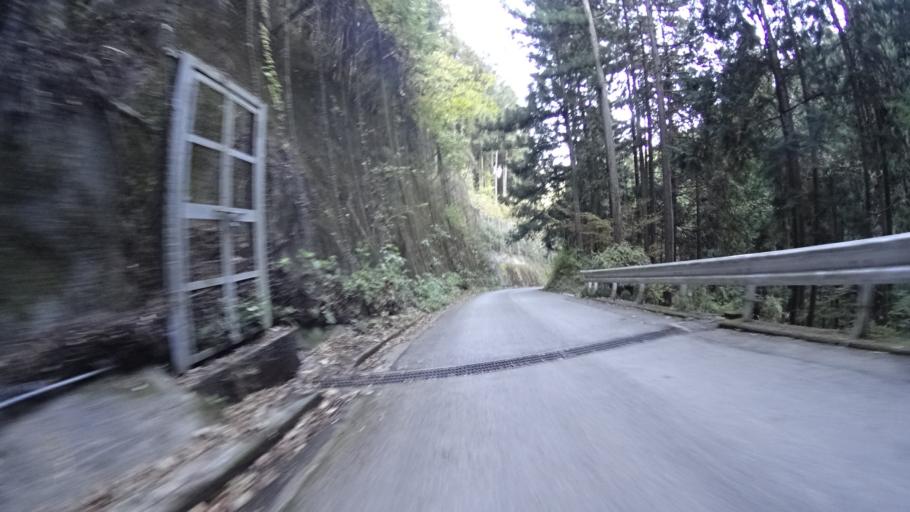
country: JP
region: Yamanashi
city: Uenohara
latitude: 35.6592
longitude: 139.1736
